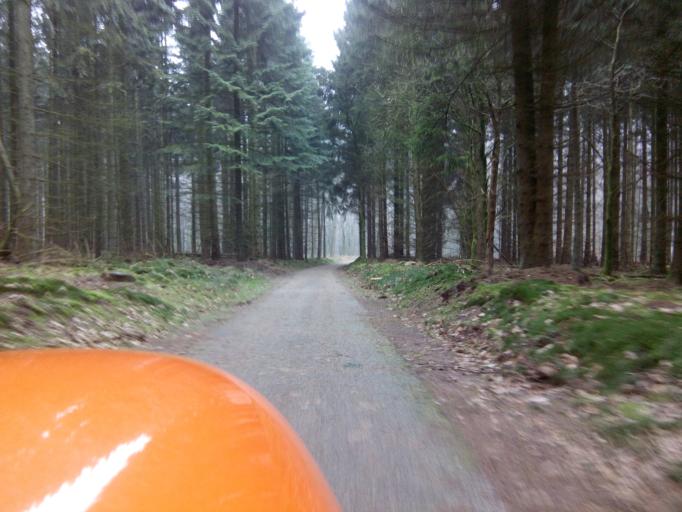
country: NL
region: Gelderland
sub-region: Gemeente Barneveld
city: Garderen
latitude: 52.2511
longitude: 5.6965
